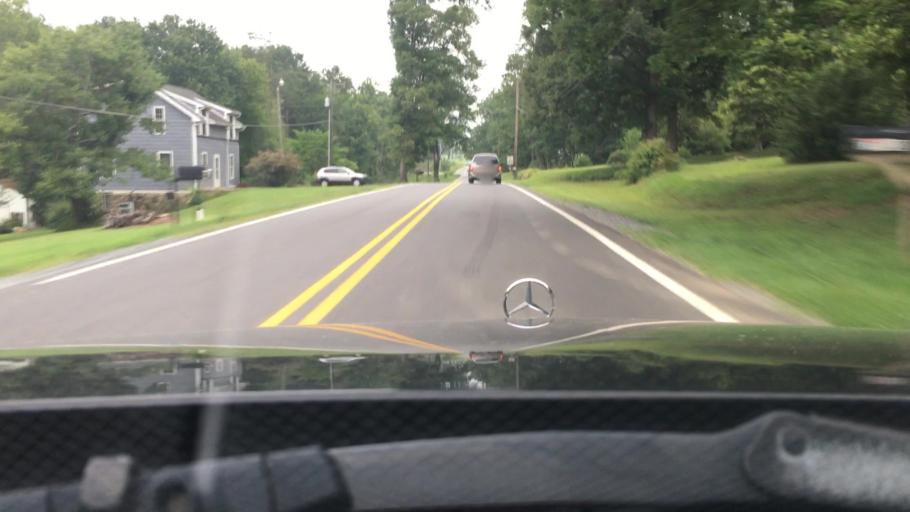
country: US
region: Virginia
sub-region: Campbell County
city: Timberlake
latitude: 37.3032
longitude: -79.2332
